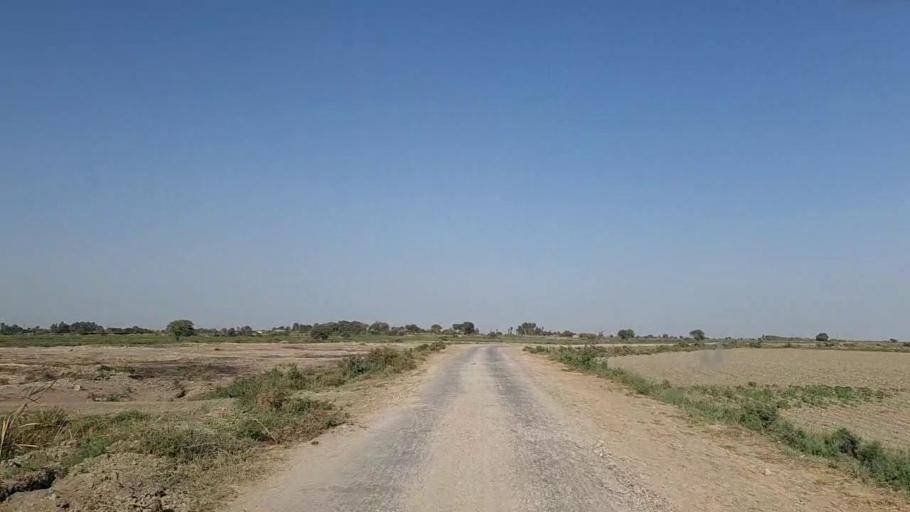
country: PK
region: Sindh
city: Chuhar Jamali
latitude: 24.5248
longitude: 68.1064
